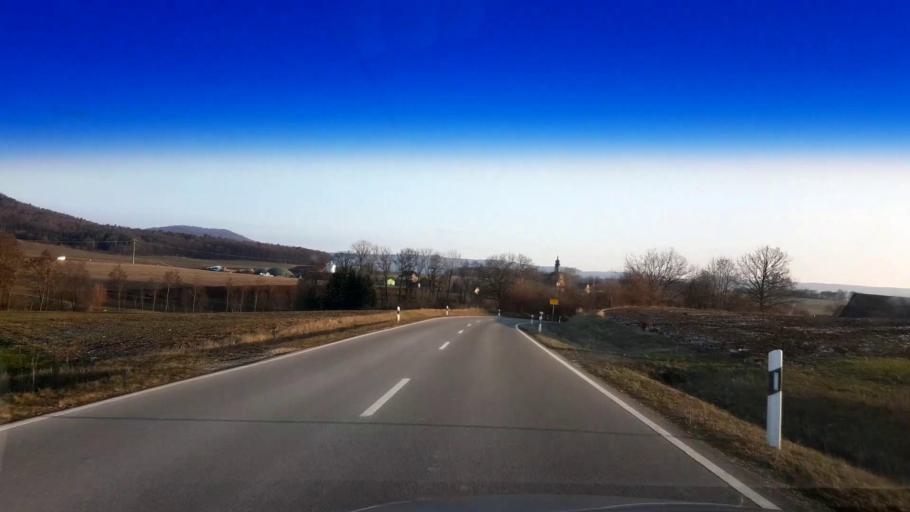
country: DE
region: Bavaria
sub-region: Upper Franconia
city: Schesslitz
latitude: 50.0071
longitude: 11.0147
